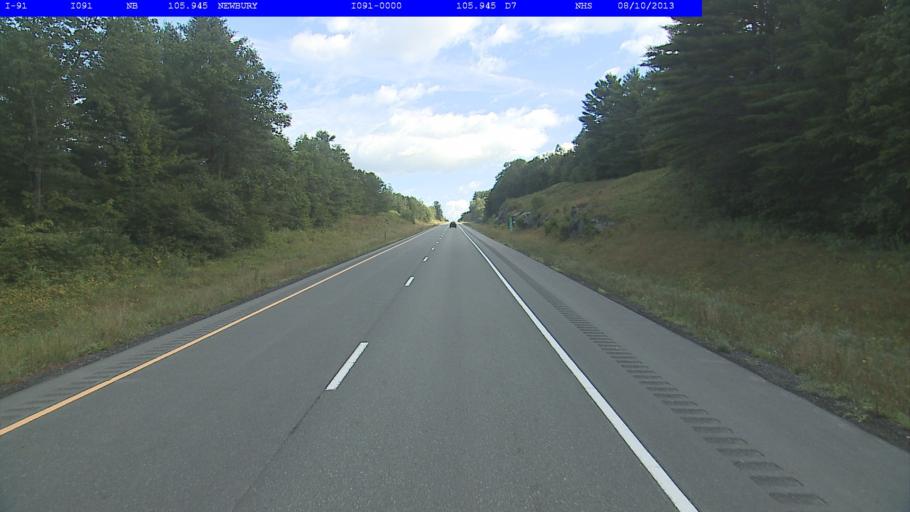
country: US
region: New Hampshire
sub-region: Grafton County
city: Haverhill
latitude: 44.0989
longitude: -72.1096
